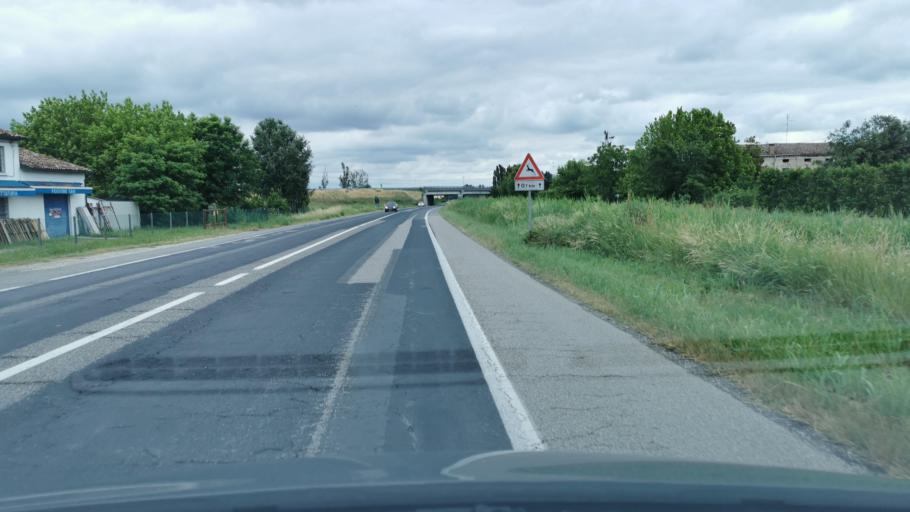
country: IT
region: Emilia-Romagna
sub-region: Provincia di Ravenna
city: Cotignola
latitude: 44.3969
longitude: 11.9596
